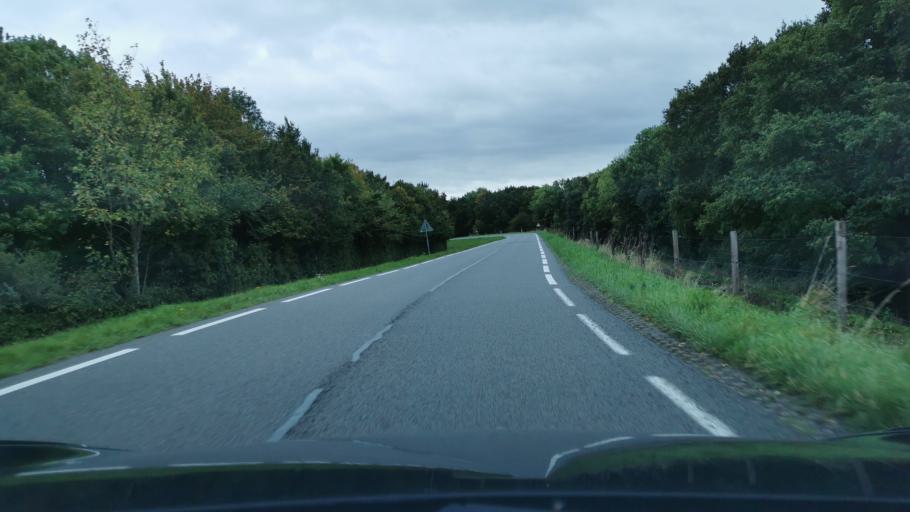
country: NL
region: Zeeland
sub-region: Gemeente Veere
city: Veere
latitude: 51.5610
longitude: 3.6424
